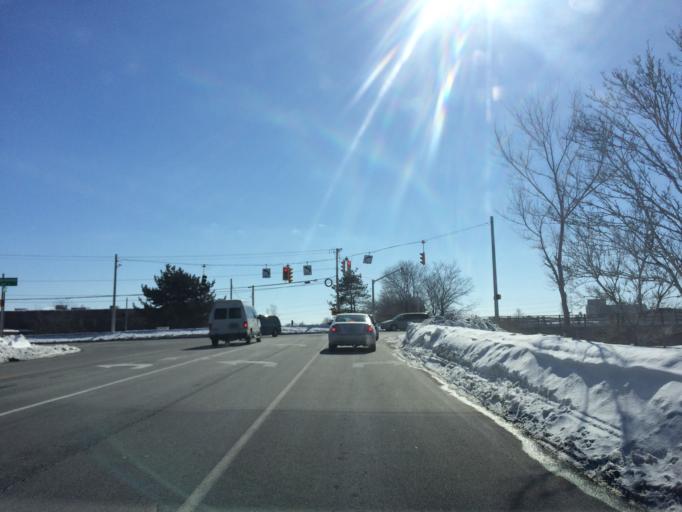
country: US
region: New York
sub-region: Monroe County
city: Rochester
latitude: 43.0957
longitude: -77.6010
